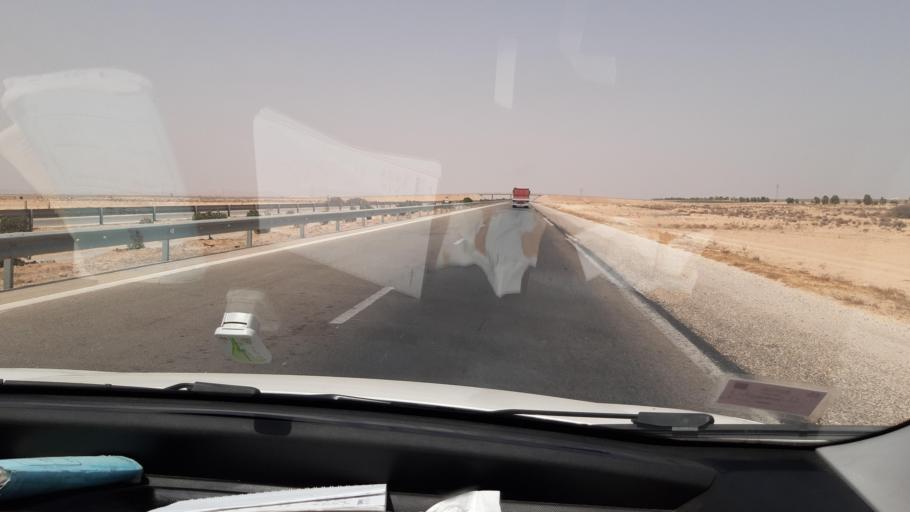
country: TN
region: Qabis
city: Gabes
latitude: 33.9274
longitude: 9.9577
